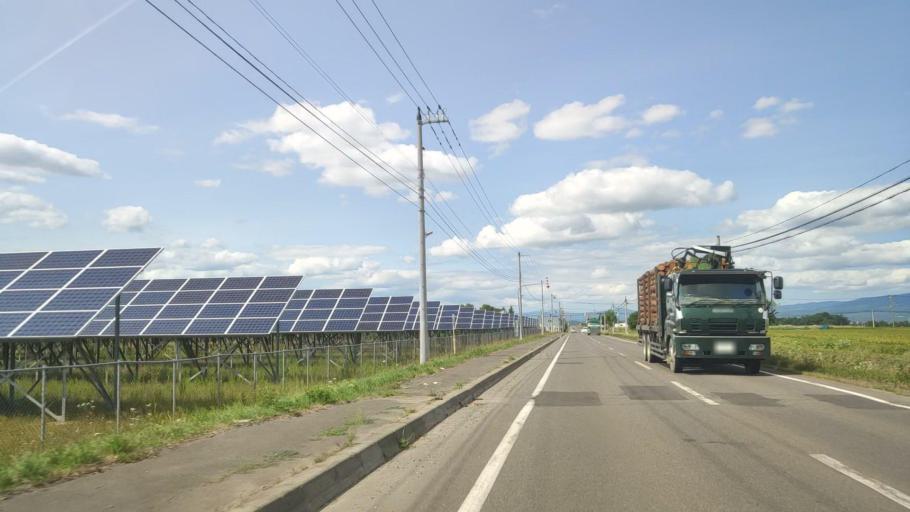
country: JP
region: Hokkaido
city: Nayoro
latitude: 44.2941
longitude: 142.4294
